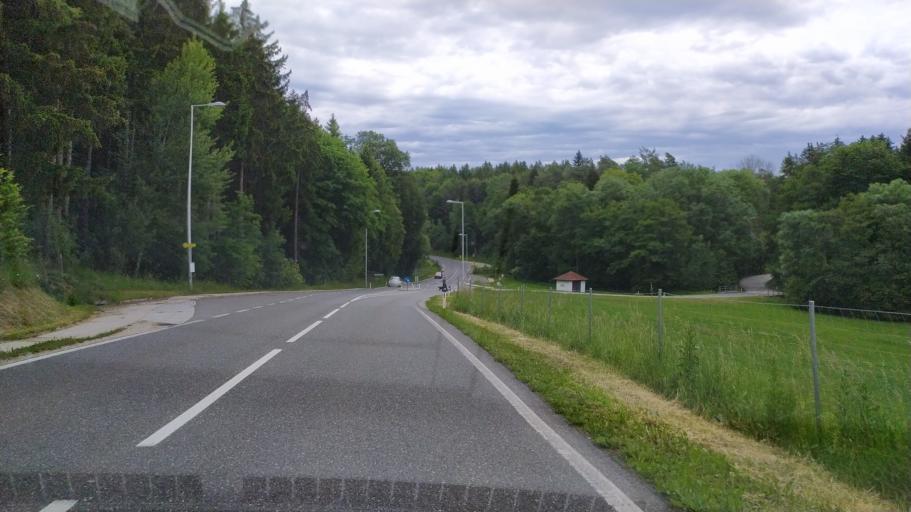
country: AT
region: Upper Austria
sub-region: Politischer Bezirk Perg
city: Perg
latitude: 48.2589
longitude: 14.6590
